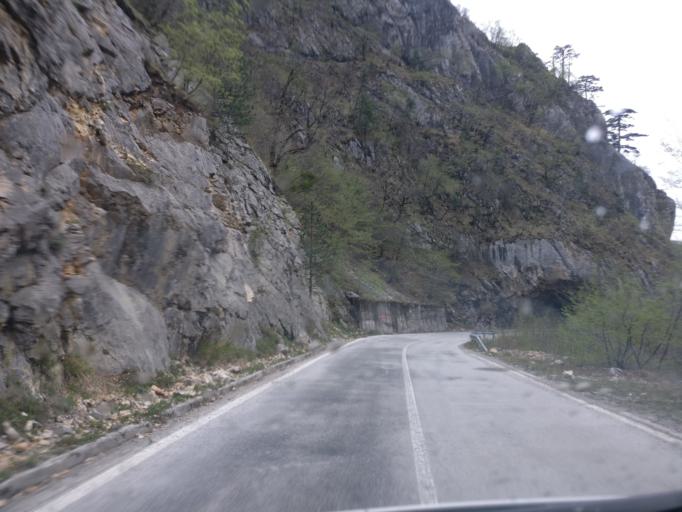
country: ME
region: Opstina Pluzine
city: Pluzine
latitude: 43.2393
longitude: 18.8420
